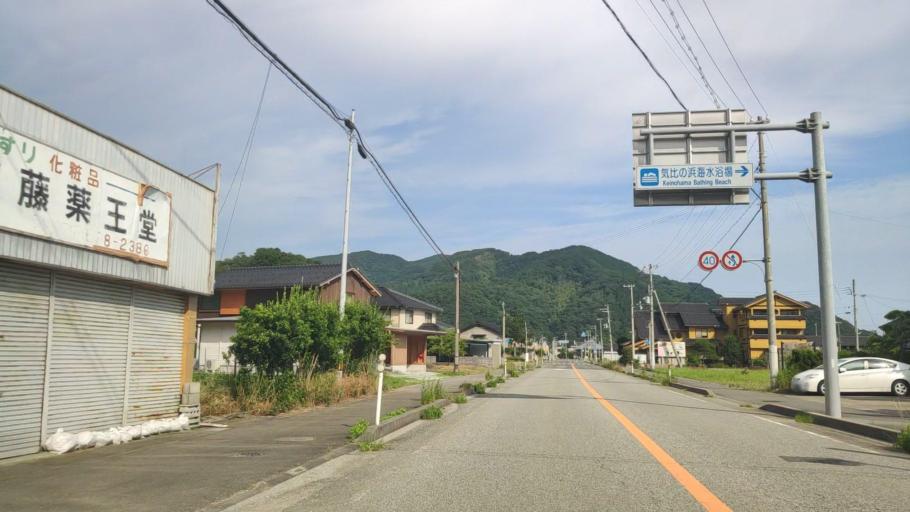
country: JP
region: Hyogo
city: Toyooka
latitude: 35.6411
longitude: 134.8351
